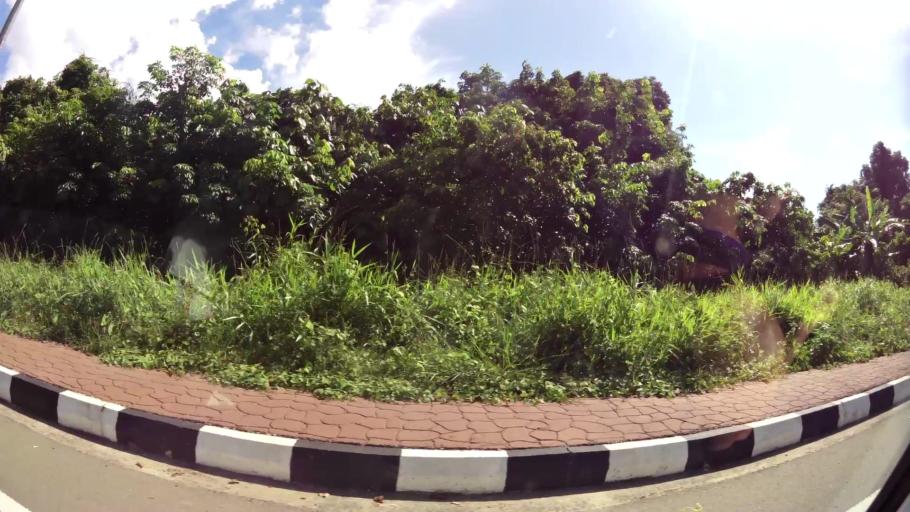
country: BN
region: Brunei and Muara
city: Bandar Seri Begawan
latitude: 4.9418
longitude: 114.9399
